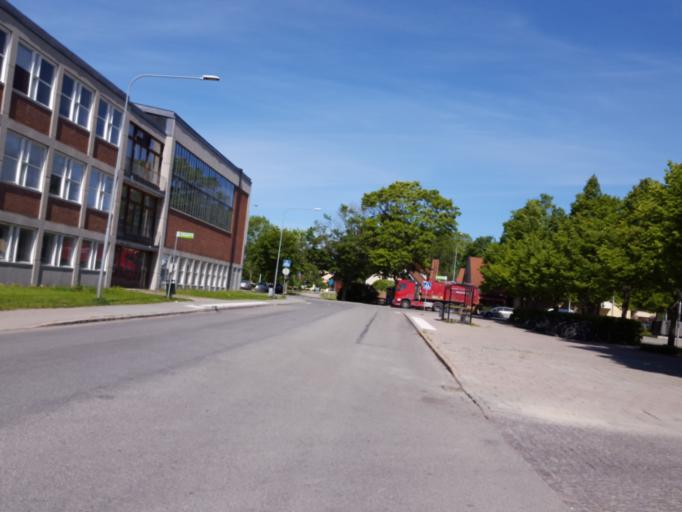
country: SE
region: Uppsala
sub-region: Uppsala Kommun
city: Uppsala
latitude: 59.8675
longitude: 17.6706
